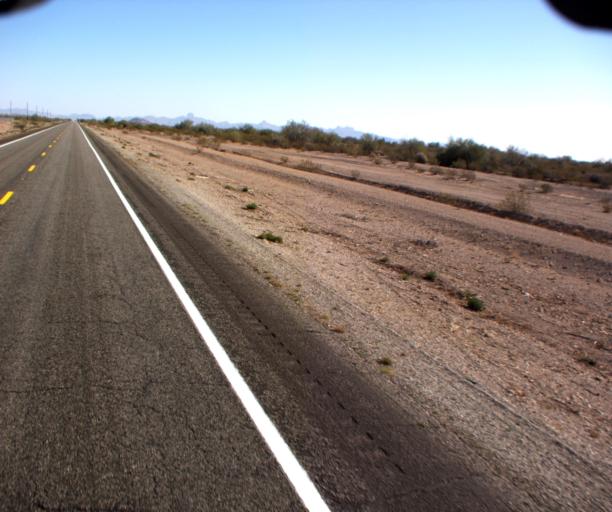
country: US
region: Arizona
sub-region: Yuma County
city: Fortuna Foothills
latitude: 32.8754
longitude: -114.3503
